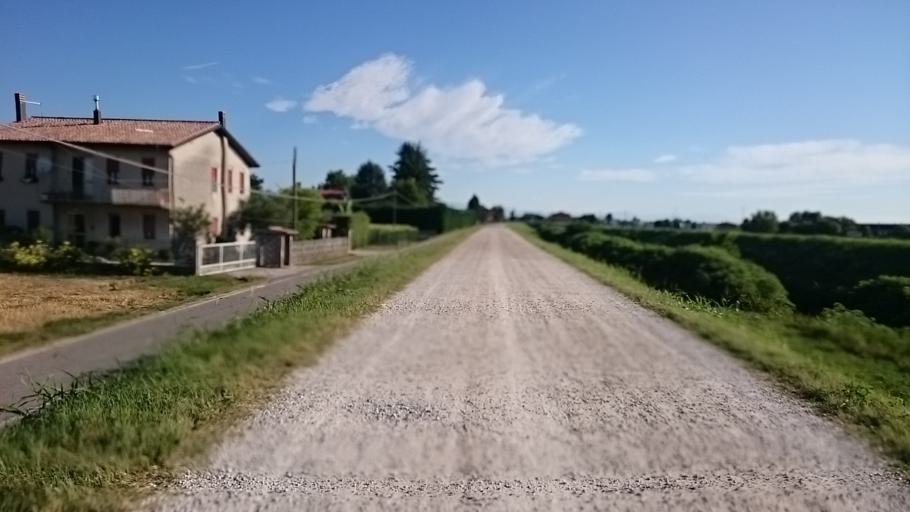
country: IT
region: Veneto
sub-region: Provincia di Padova
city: Mejaniga
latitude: 45.4786
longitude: 11.8978
